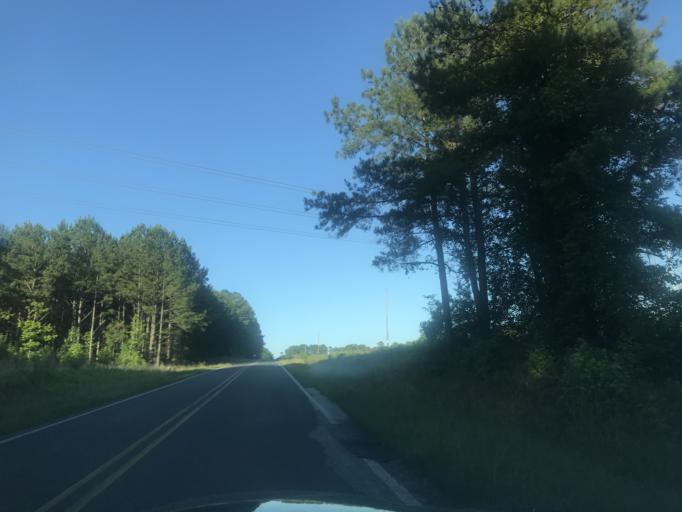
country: US
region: North Carolina
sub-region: Johnston County
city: Archer Lodge
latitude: 35.7301
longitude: -78.4162
